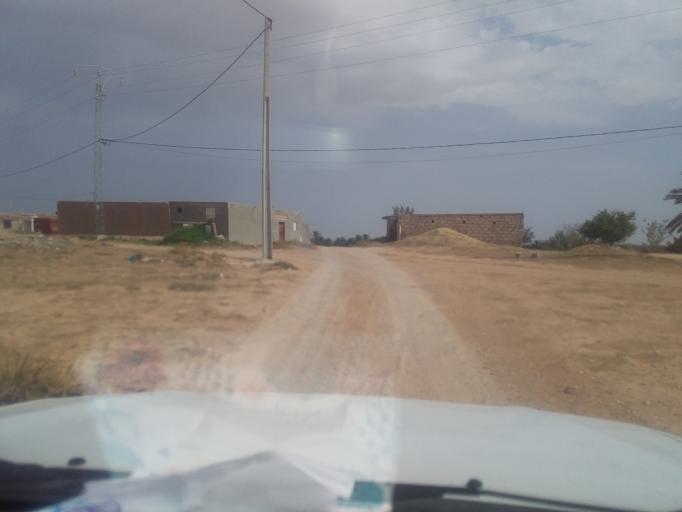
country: TN
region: Madanin
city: Medenine
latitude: 33.5828
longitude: 10.3293
